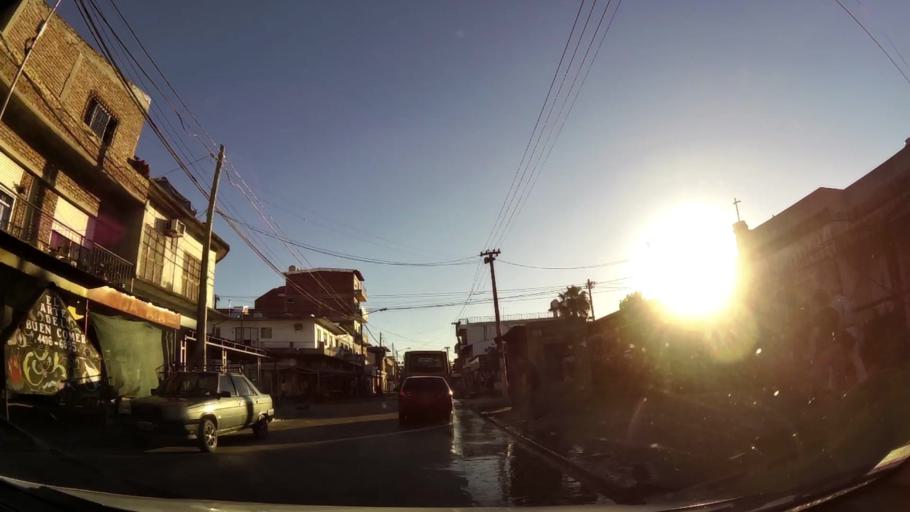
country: AR
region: Buenos Aires
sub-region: Partido de Moron
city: Moron
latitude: -34.7126
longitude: -58.6118
